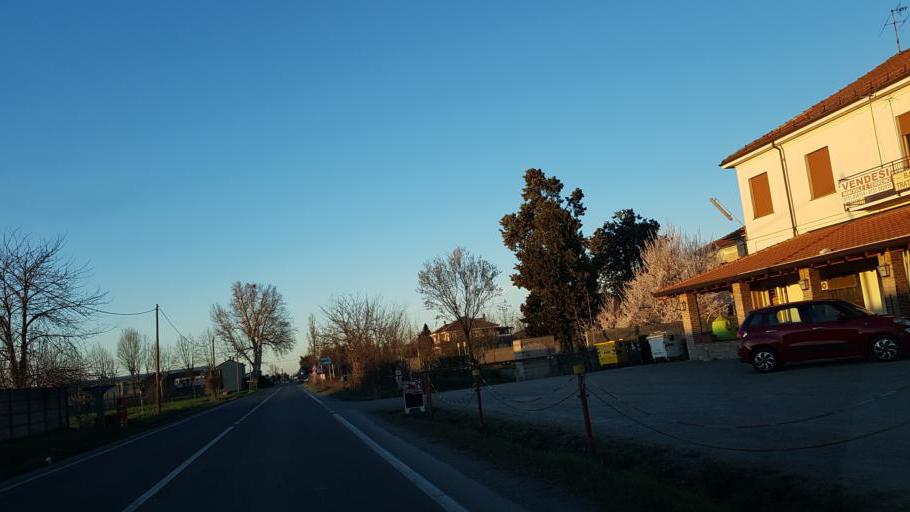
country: IT
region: Piedmont
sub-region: Provincia di Alessandria
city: Carbonara Scrivia
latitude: 44.8618
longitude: 8.8555
